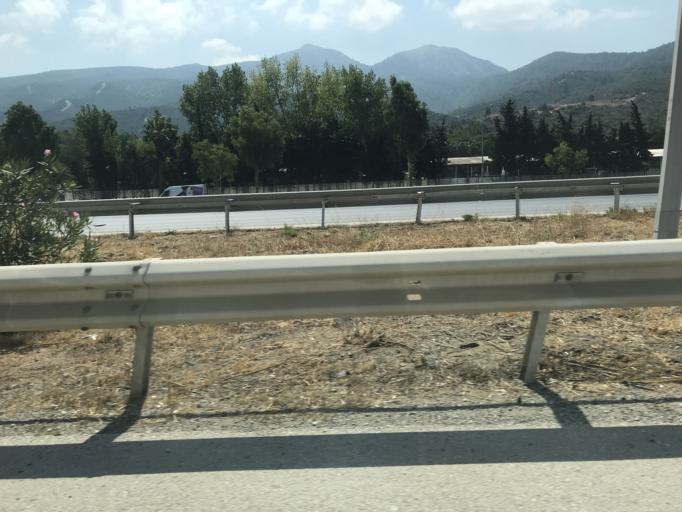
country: TR
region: Izmir
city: Karsiyaka
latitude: 38.3901
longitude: 26.9531
